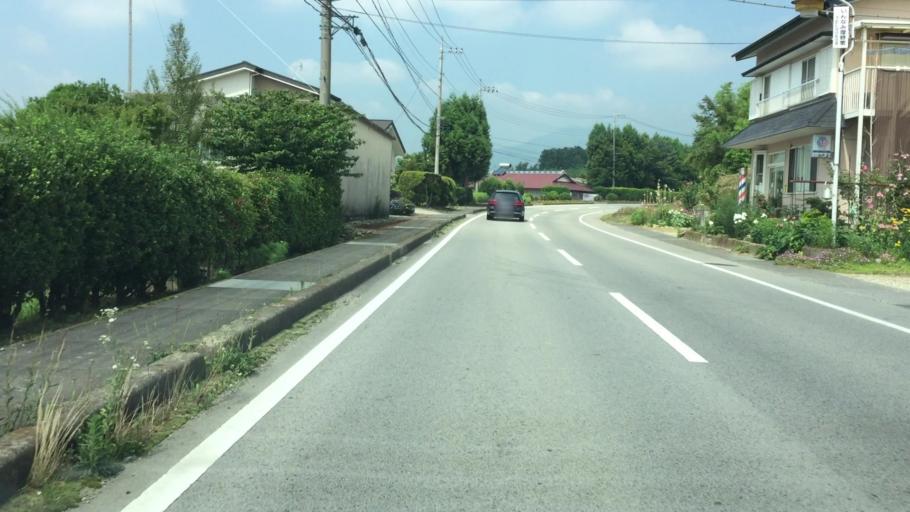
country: JP
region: Tochigi
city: Kuroiso
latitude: 36.9725
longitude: 139.9669
